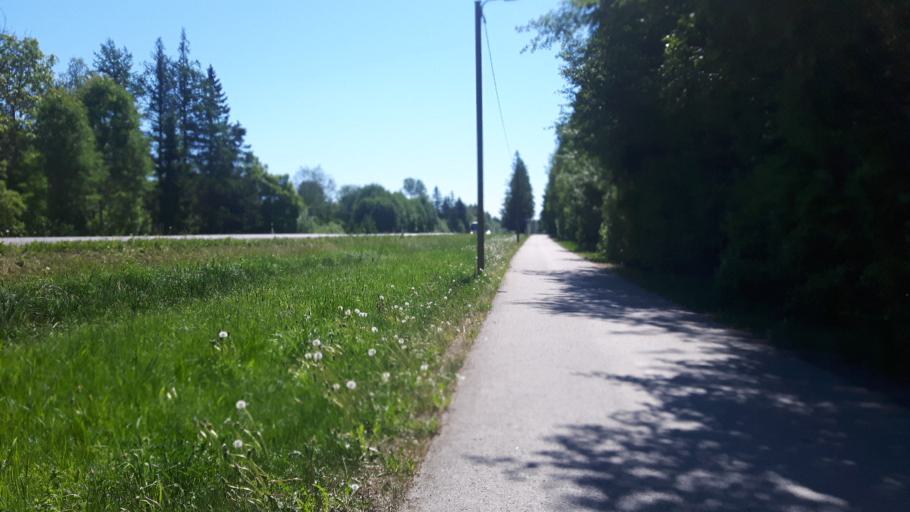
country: EE
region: Harju
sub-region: Saku vald
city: Saku
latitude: 59.2860
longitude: 24.6626
